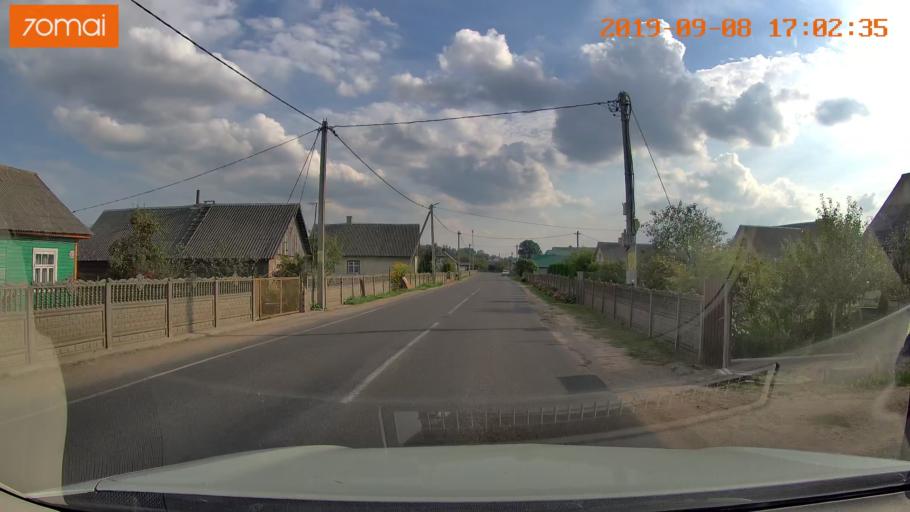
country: BY
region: Grodnenskaya
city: Hrodna
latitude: 53.7024
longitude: 23.9401
